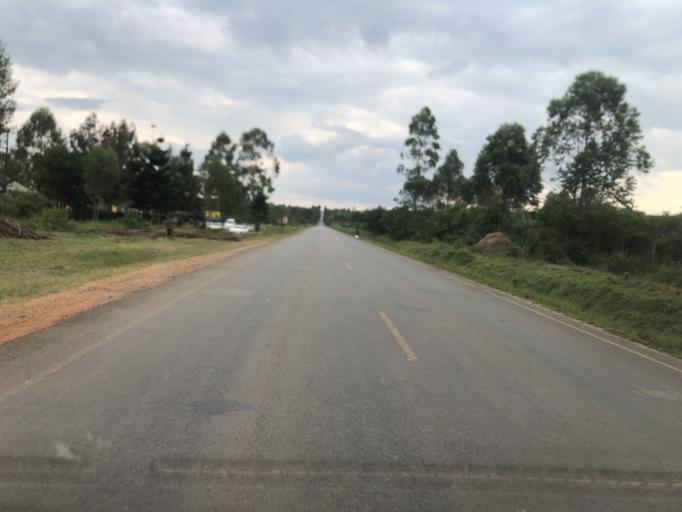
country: UG
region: Western Region
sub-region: Sheema District
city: Kibingo
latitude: -0.5792
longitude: 30.4216
